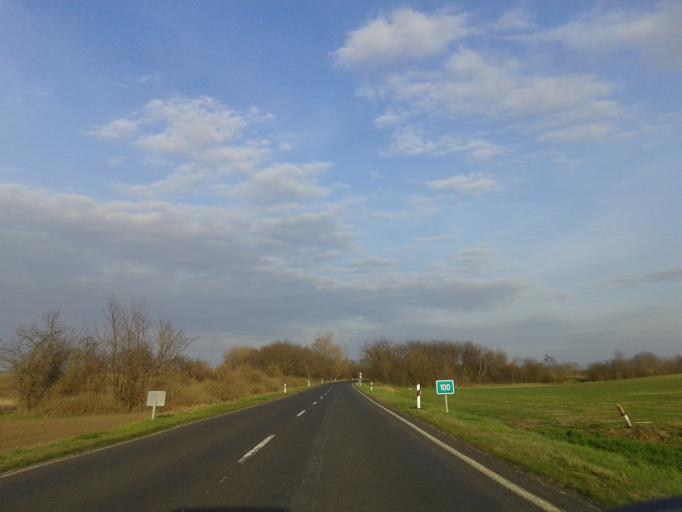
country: HU
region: Komarom-Esztergom
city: Acs
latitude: 47.7393
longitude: 17.9568
